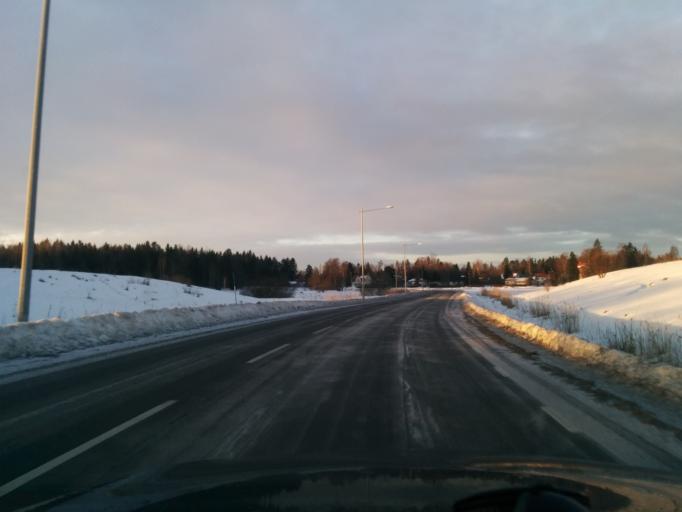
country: SE
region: Uppsala
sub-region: Tierps Kommun
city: Orbyhus
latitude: 60.2233
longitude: 17.7071
